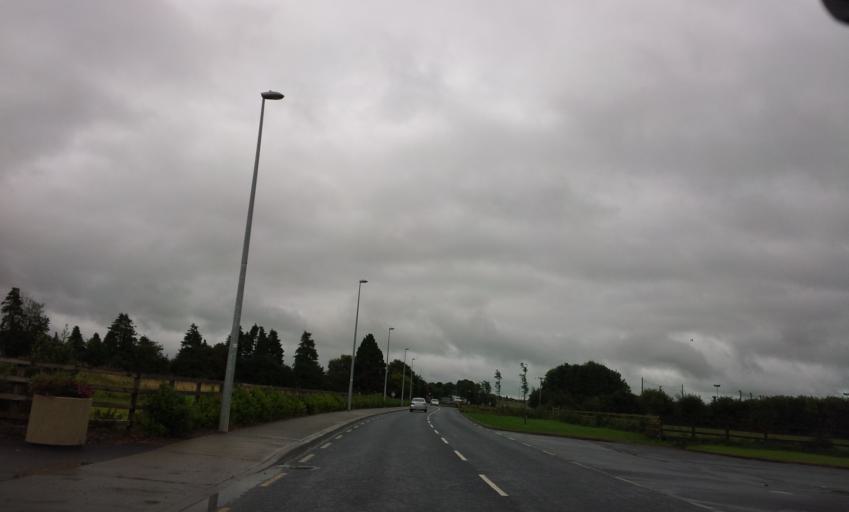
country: IE
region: Munster
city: Cashel
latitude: 52.5124
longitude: -7.8794
